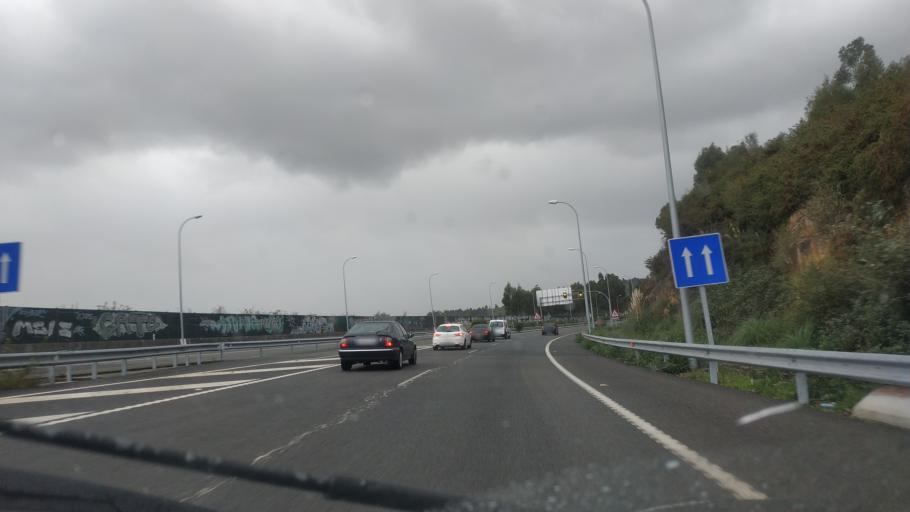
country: ES
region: Galicia
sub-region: Provincia da Coruna
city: Culleredo
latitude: 43.3215
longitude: -8.4091
